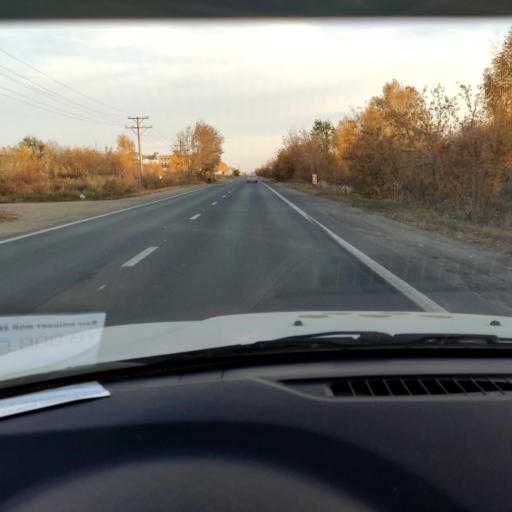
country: RU
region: Samara
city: Tol'yatti
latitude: 53.5548
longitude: 49.3661
